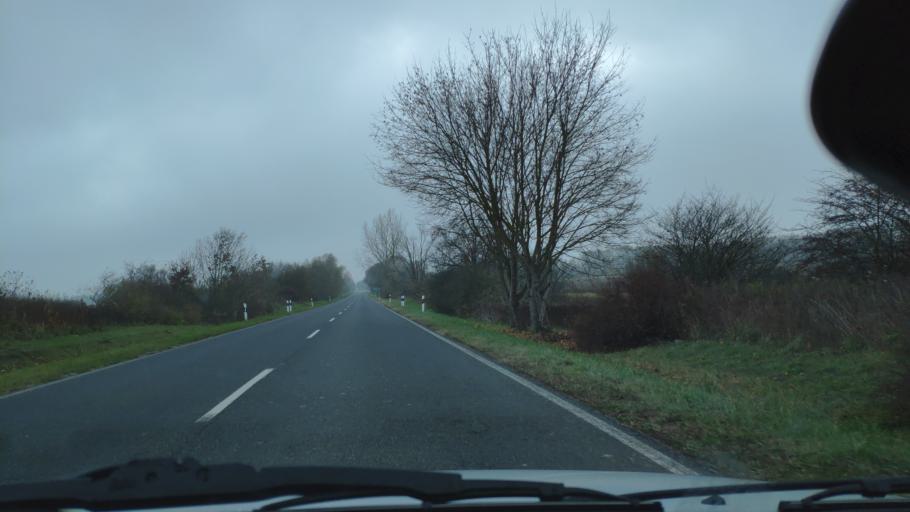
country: HU
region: Somogy
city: Balatonbereny
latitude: 46.6084
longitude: 17.2721
